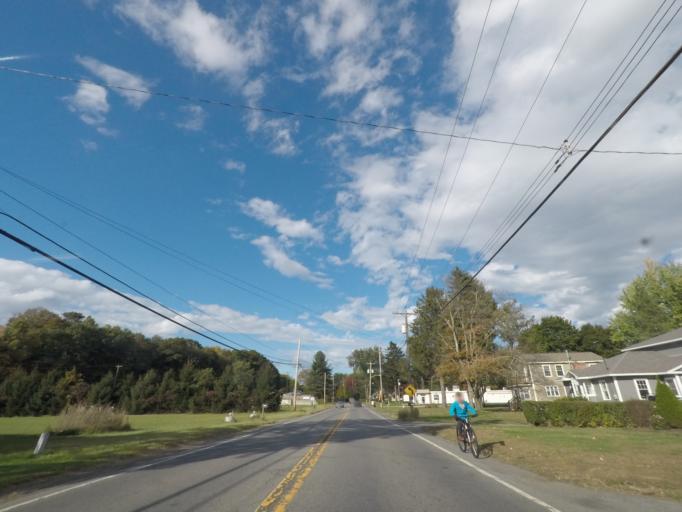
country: US
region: New York
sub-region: Schenectady County
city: Rotterdam
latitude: 42.7475
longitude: -73.9421
